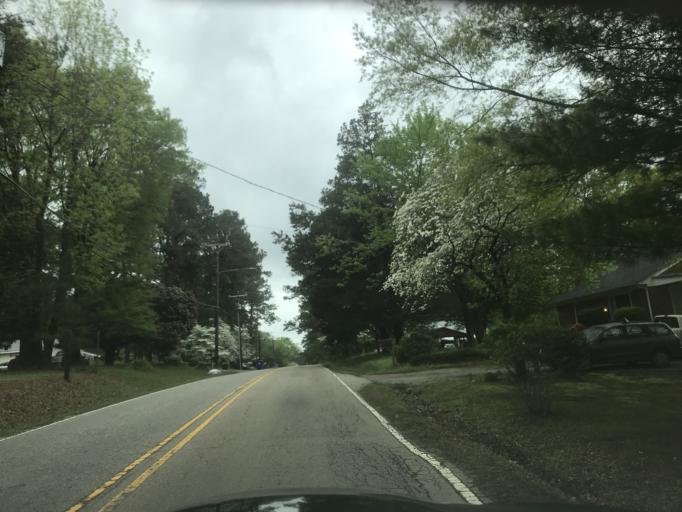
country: US
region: North Carolina
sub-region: Wake County
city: Raleigh
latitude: 35.7472
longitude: -78.6576
